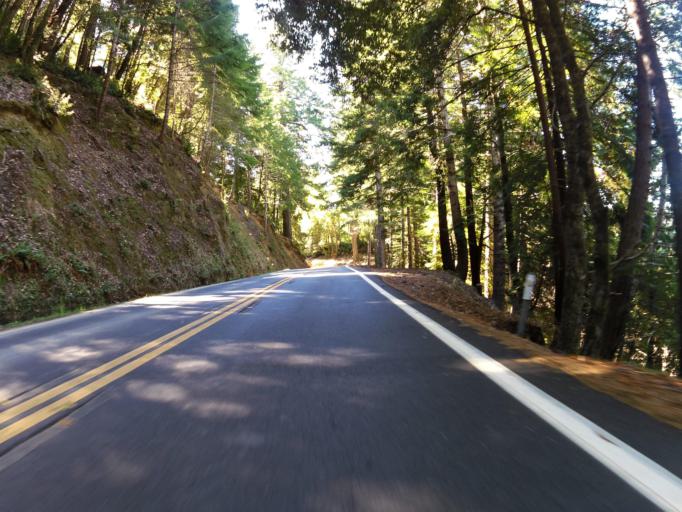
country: US
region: California
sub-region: Humboldt County
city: Redway
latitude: 39.8239
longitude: -123.7804
